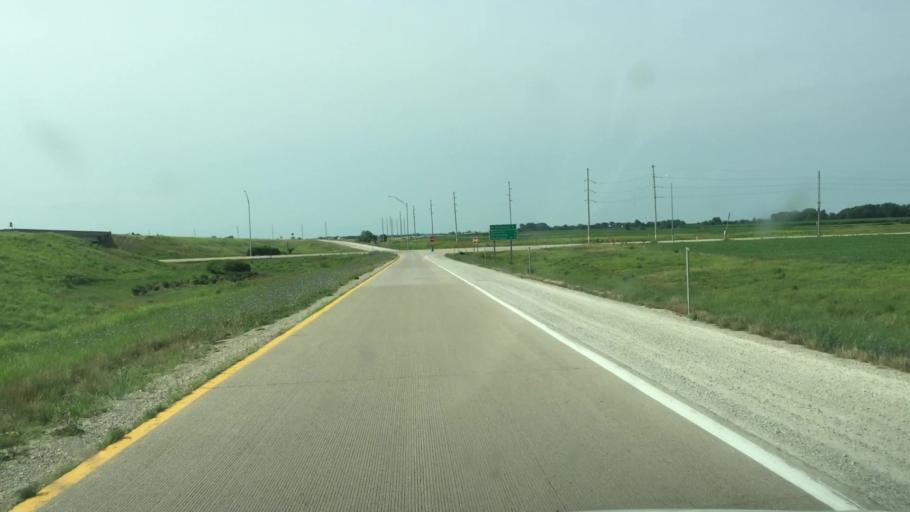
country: US
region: Illinois
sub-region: Hancock County
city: Nauvoo
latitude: 40.6409
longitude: -91.5572
